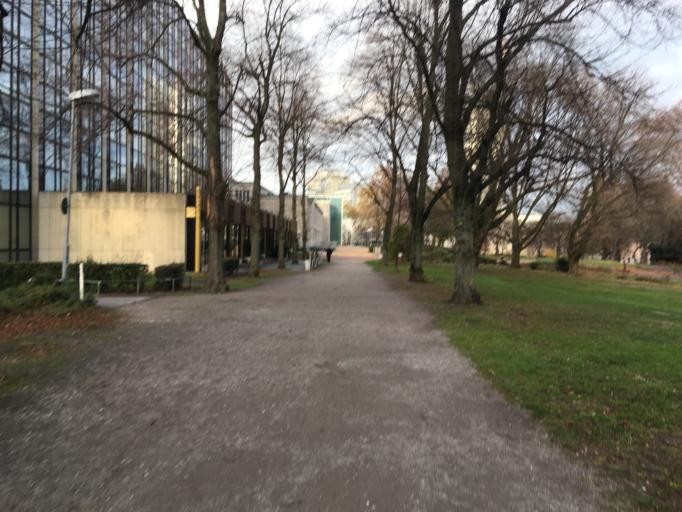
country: DE
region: North Rhine-Westphalia
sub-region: Regierungsbezirk Dusseldorf
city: Essen
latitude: 51.4445
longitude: 7.0102
